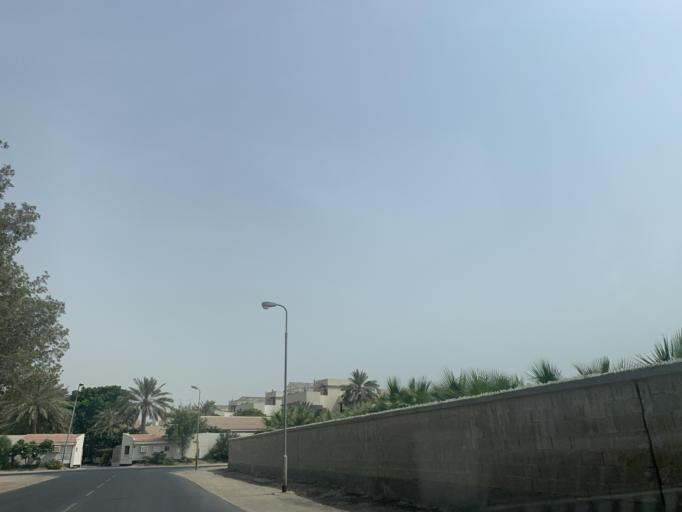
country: BH
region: Manama
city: Jidd Hafs
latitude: 26.2016
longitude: 50.4725
